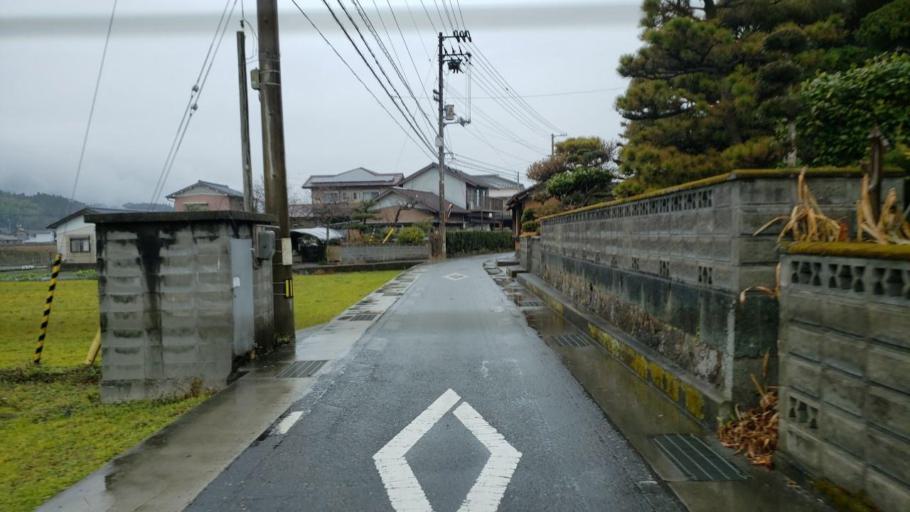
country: JP
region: Tokushima
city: Kamojimacho-jogejima
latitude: 34.0573
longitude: 134.3005
